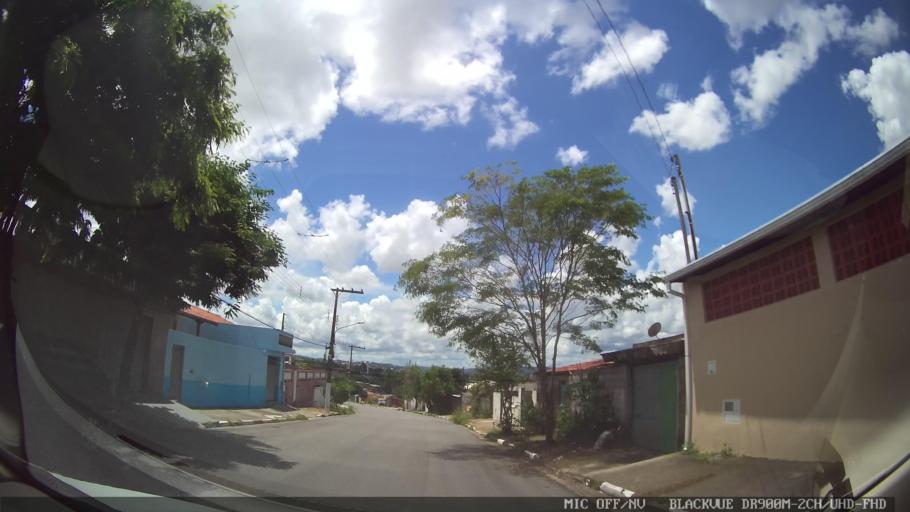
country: BR
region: Sao Paulo
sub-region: Braganca Paulista
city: Braganca Paulista
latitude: -22.9339
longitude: -46.5658
